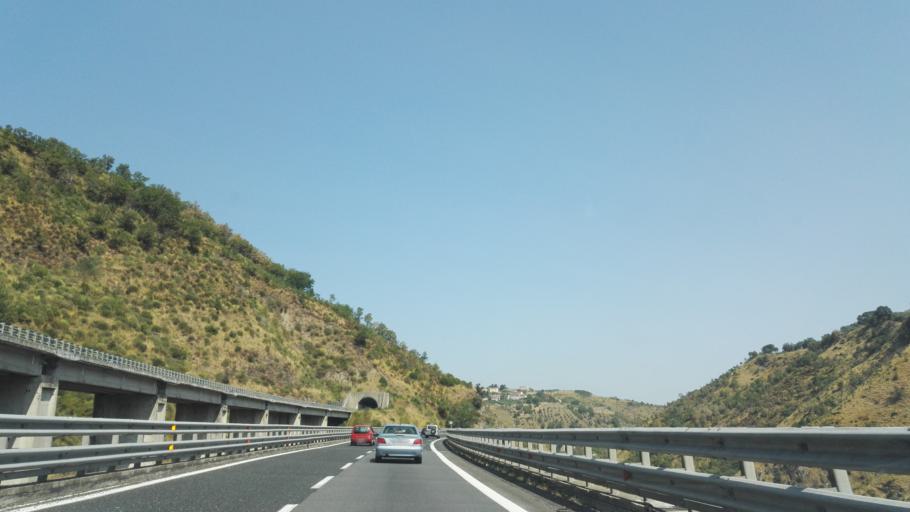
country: IT
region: Calabria
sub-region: Provincia di Cosenza
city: Laurignano
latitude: 39.2613
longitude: 16.2522
